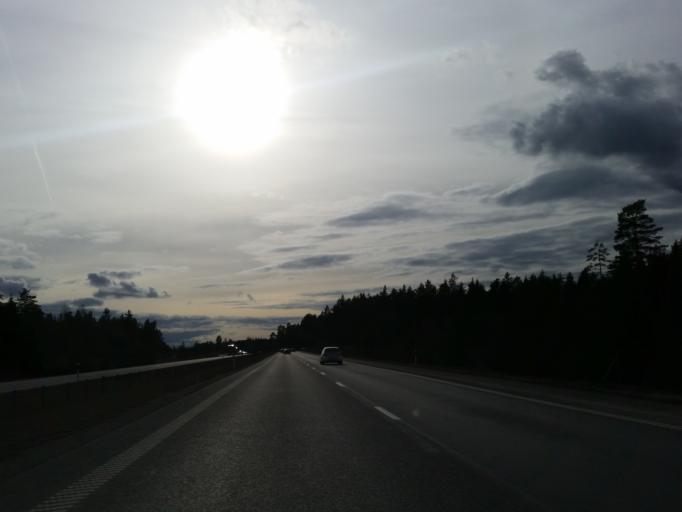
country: SE
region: OEstergoetland
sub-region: Norrkopings Kommun
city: Krokek
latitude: 58.7214
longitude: 16.3841
